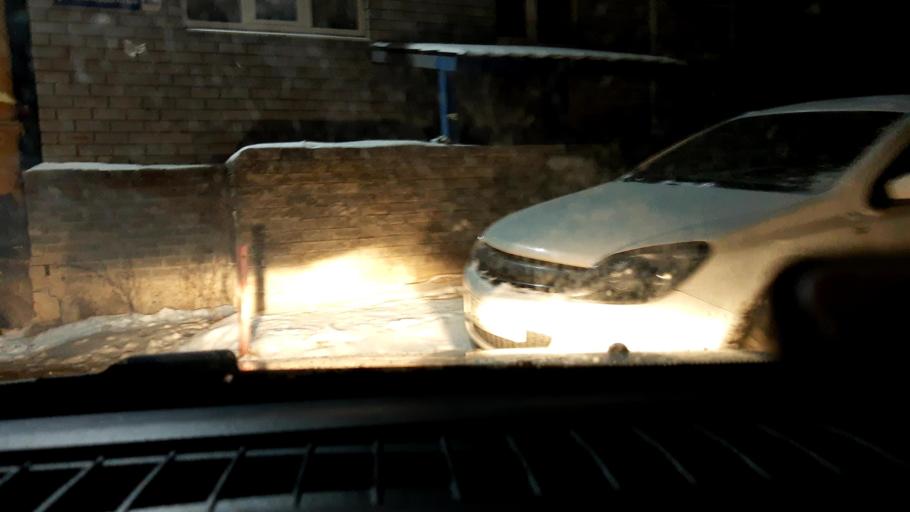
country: RU
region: Nizjnij Novgorod
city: Bogorodsk
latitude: 56.1064
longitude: 43.5125
